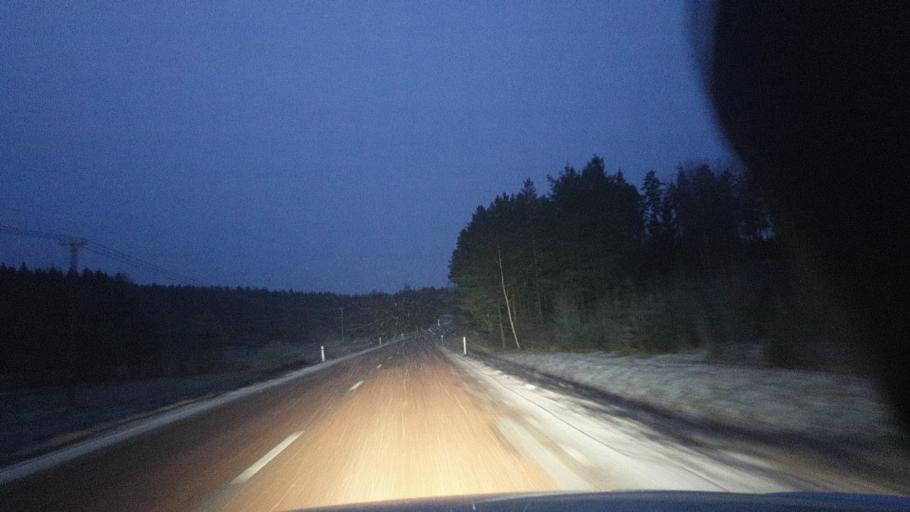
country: SE
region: Vaermland
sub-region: Arvika Kommun
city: Arvika
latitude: 59.6105
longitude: 12.6189
